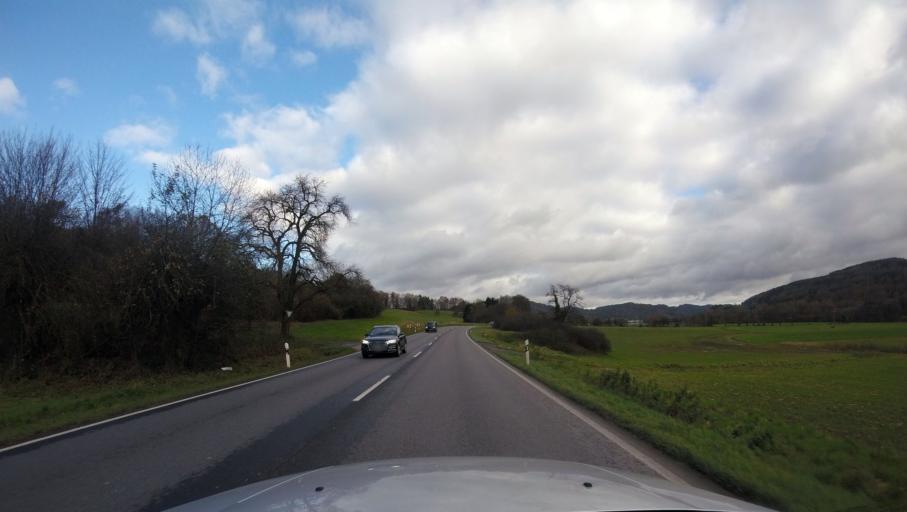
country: DE
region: Baden-Wuerttemberg
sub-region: Regierungsbezirk Stuttgart
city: Sulzbach an der Murr
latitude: 48.9991
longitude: 9.4796
